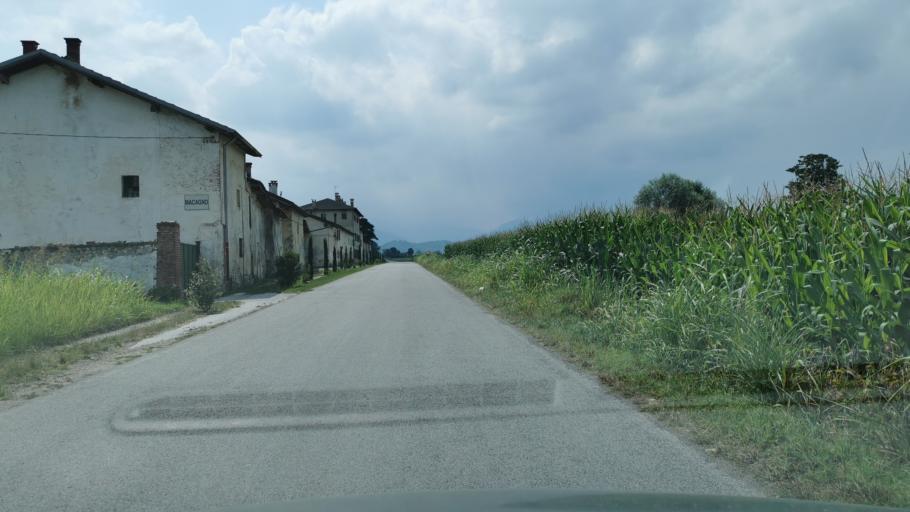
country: IT
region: Piedmont
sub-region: Provincia di Cuneo
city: San Rocco
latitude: 44.4301
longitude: 7.4833
